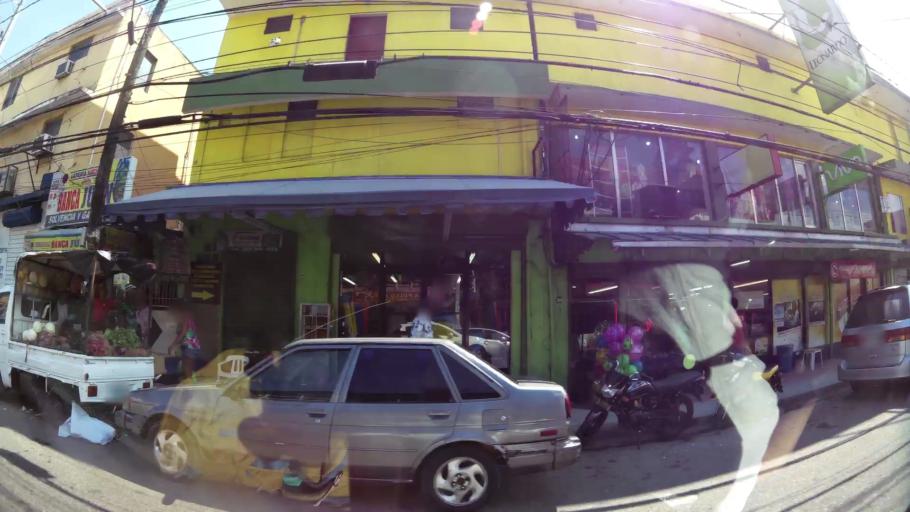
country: DO
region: Nacional
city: Santo Domingo
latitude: 18.4766
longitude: -69.9743
